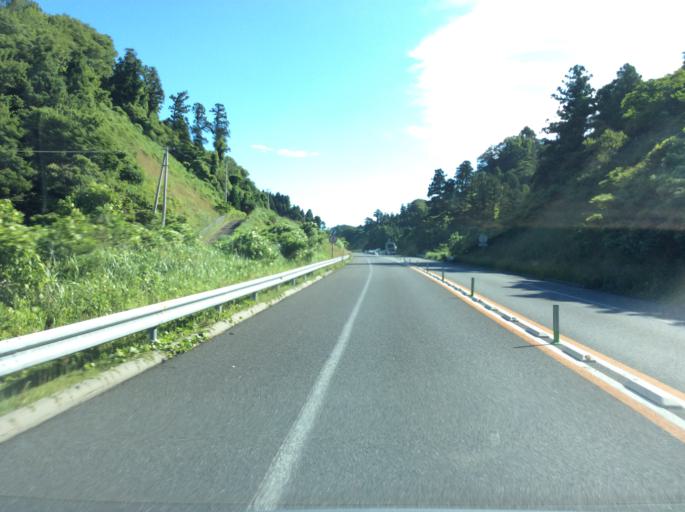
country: JP
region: Fukushima
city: Iwaki
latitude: 37.1826
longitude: 140.9813
